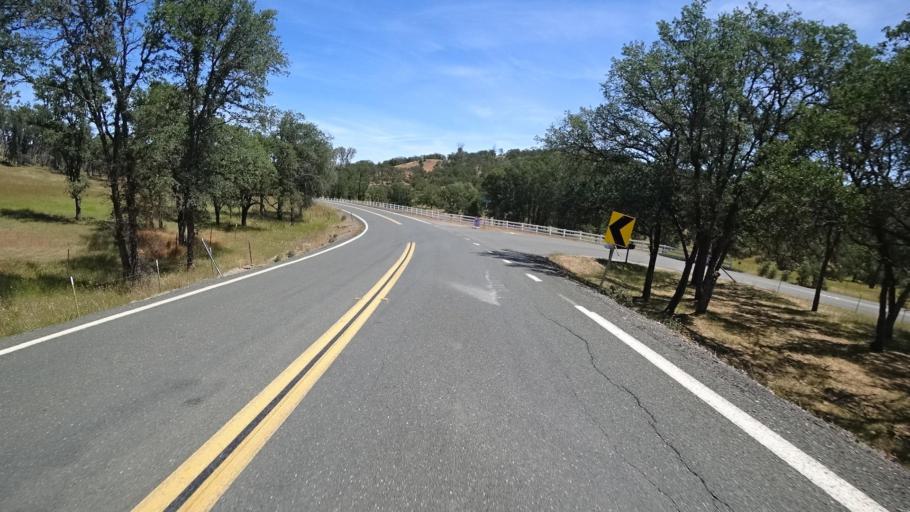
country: US
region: California
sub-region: Lake County
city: Middletown
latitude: 38.7228
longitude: -122.5428
